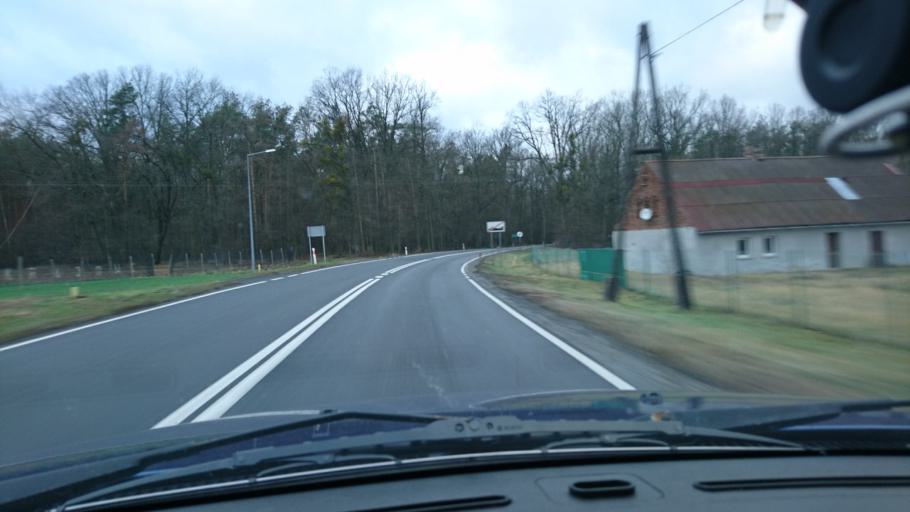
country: PL
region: Opole Voivodeship
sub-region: Powiat kluczborski
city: Kluczbork
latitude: 50.9474
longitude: 18.3161
